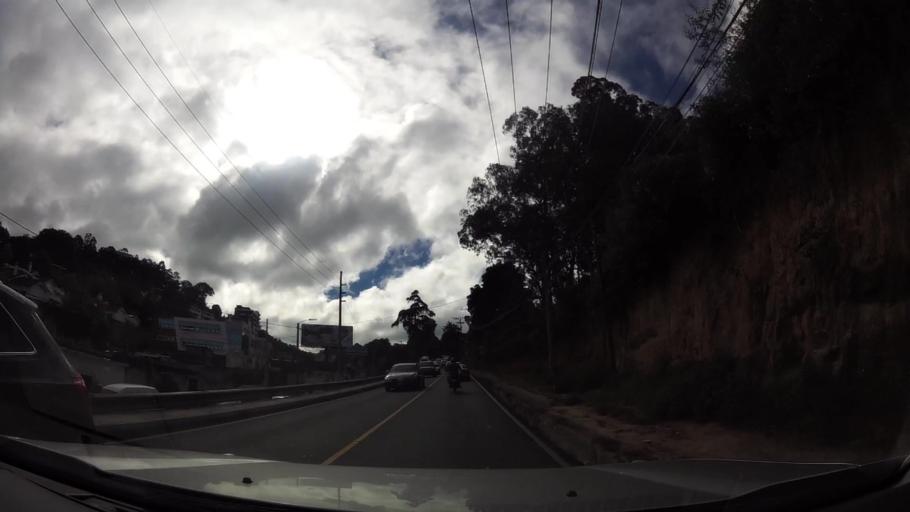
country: GT
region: Guatemala
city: Santa Catarina Pinula
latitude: 14.5737
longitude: -90.4892
